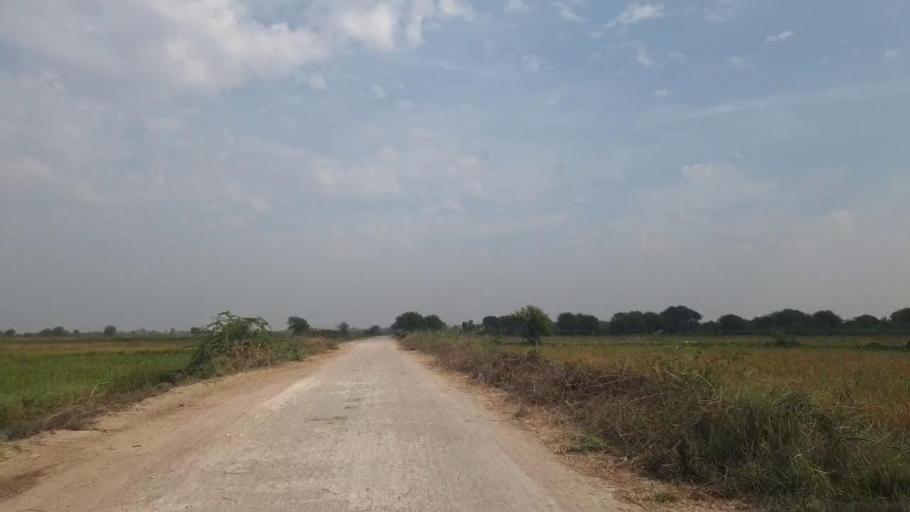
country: PK
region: Sindh
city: Rajo Khanani
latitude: 24.9574
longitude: 68.9929
